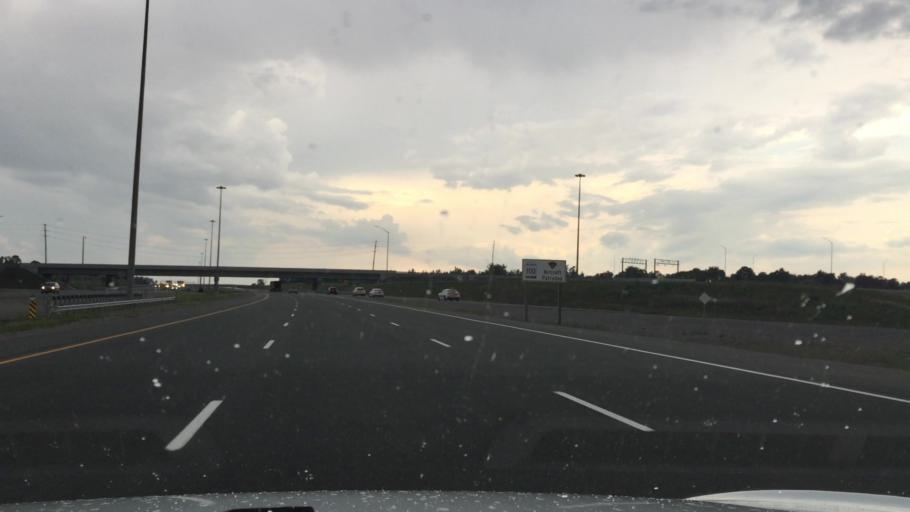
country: CA
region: Ontario
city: Ajax
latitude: 43.9506
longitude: -79.0170
